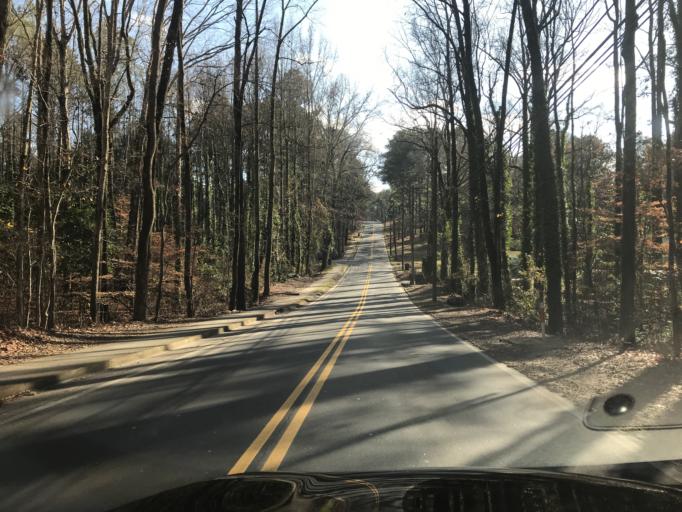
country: US
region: Georgia
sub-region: Fulton County
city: College Park
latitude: 33.6457
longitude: -84.4727
